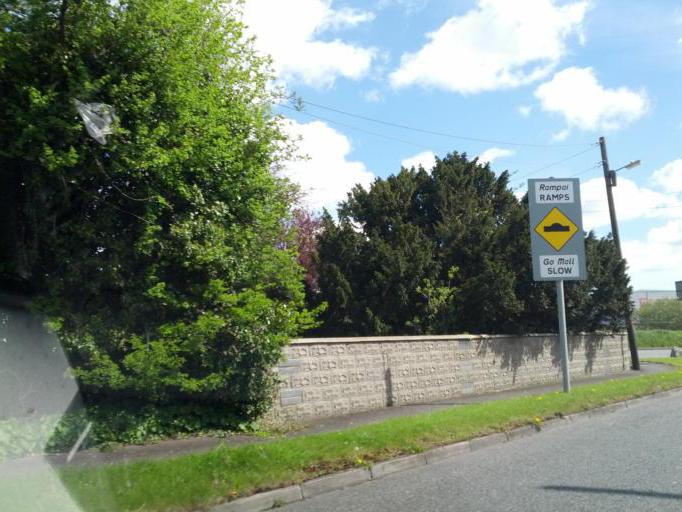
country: IE
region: Leinster
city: Ballyfermot
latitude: 53.3242
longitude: -6.3574
